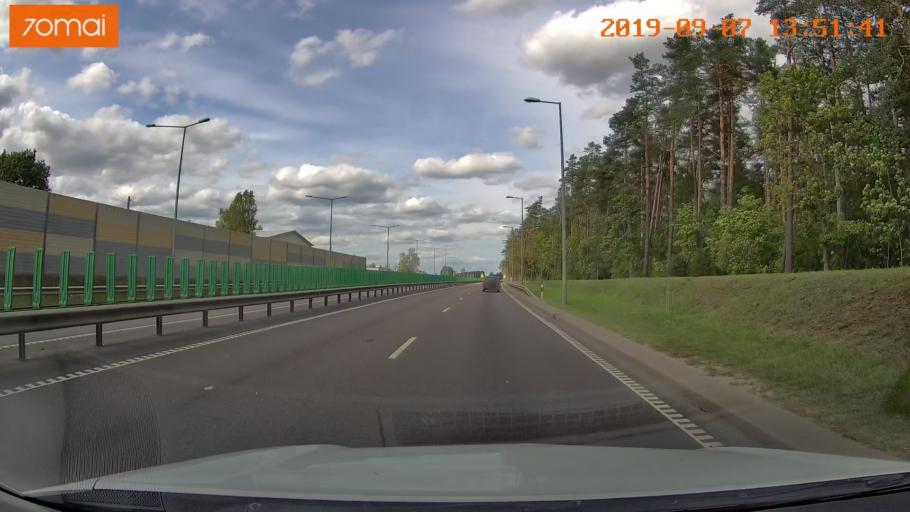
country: LT
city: Baltoji Voke
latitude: 54.6183
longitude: 25.1609
